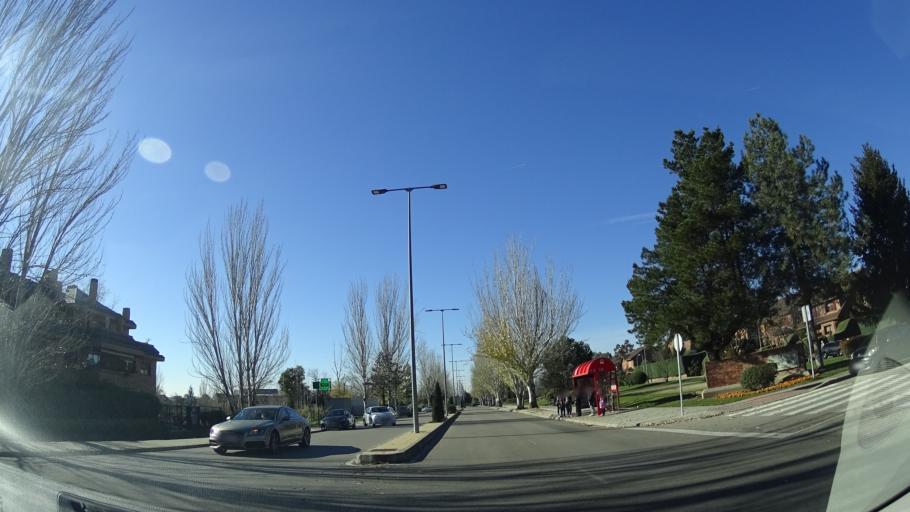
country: ES
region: Madrid
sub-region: Provincia de Madrid
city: Las Matas
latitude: 40.5362
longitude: -3.8963
